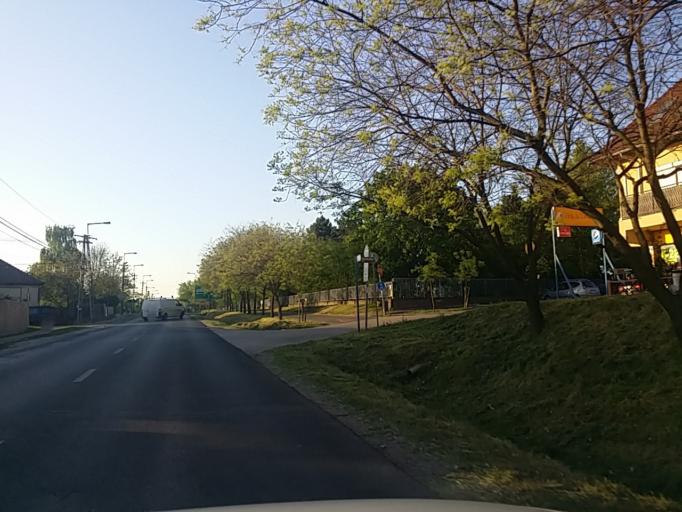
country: HU
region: Pest
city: Dunakeszi
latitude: 47.6251
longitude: 19.1559
